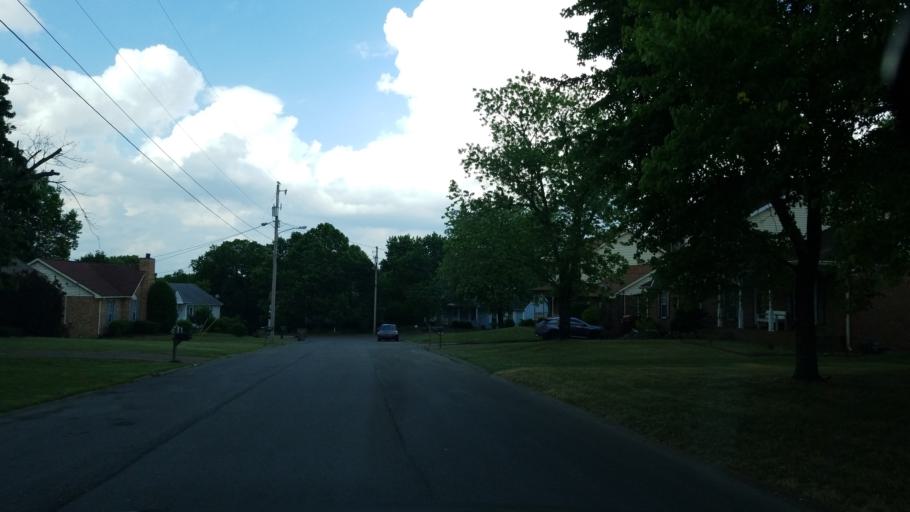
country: US
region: Tennessee
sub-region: Rutherford County
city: La Vergne
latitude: 36.0757
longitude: -86.5989
